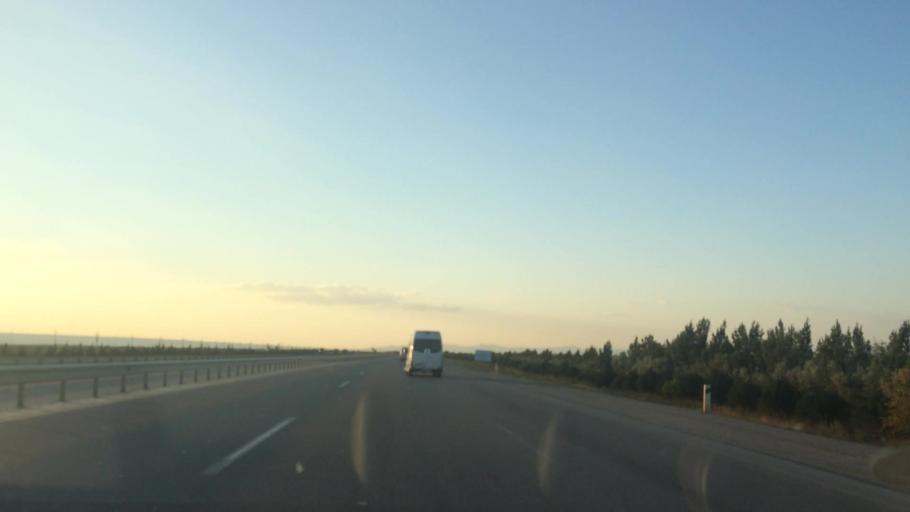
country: AZ
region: Baki
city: Qobustan
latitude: 39.9767
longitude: 49.2452
